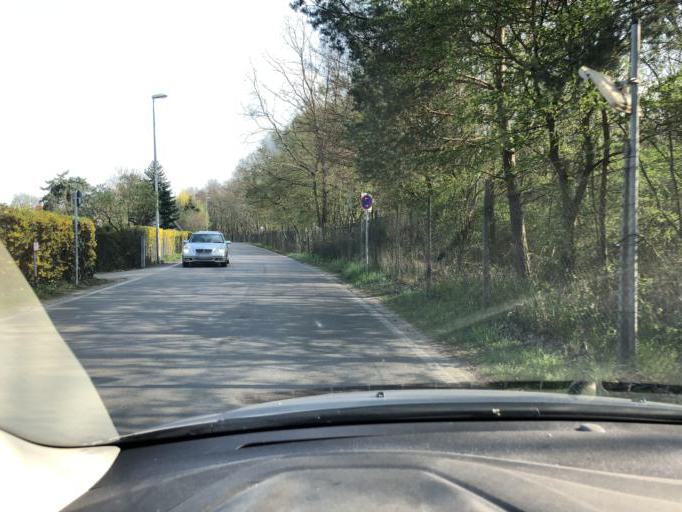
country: DE
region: Saxony
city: Taucha
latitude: 51.3732
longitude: 12.4563
